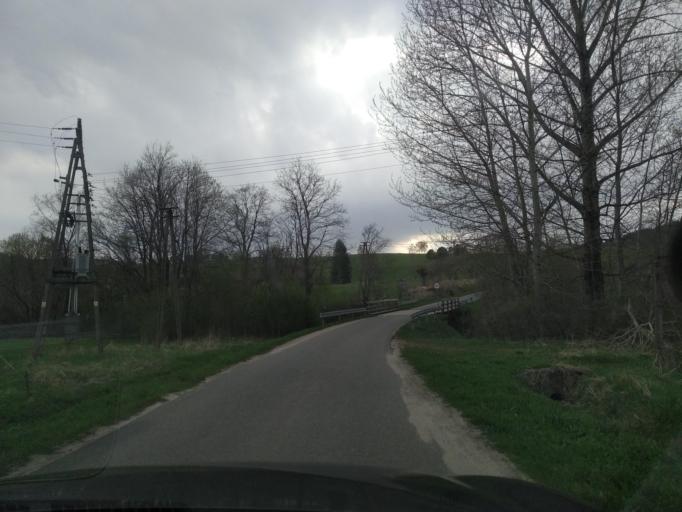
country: PL
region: Subcarpathian Voivodeship
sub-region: Powiat leski
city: Baligrod
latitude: 49.3581
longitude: 22.2047
